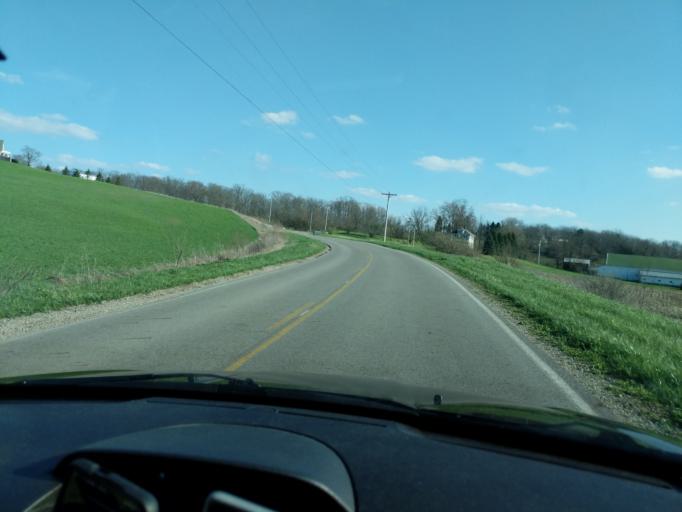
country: US
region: Ohio
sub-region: Champaign County
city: Urbana
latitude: 40.1025
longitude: -83.6662
